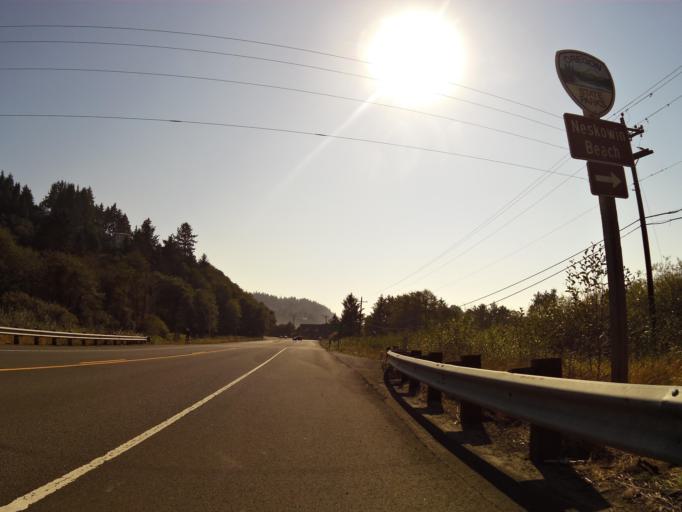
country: US
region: Oregon
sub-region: Tillamook County
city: Pacific City
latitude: 45.1049
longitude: -123.9794
